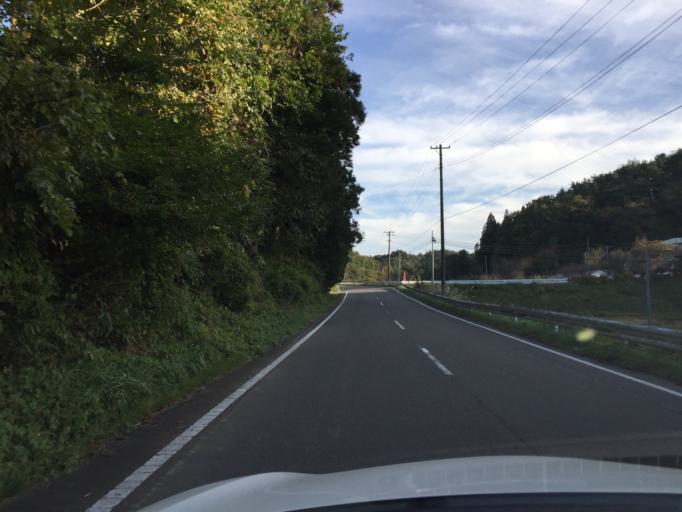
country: JP
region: Fukushima
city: Ishikawa
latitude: 37.1909
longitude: 140.5413
